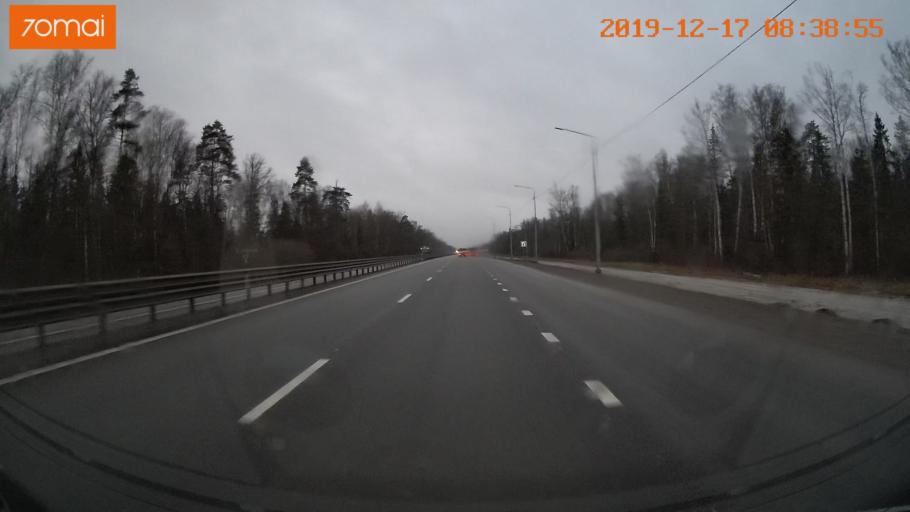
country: RU
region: Vladimir
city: Lakinsk
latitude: 55.9778
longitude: 39.8224
